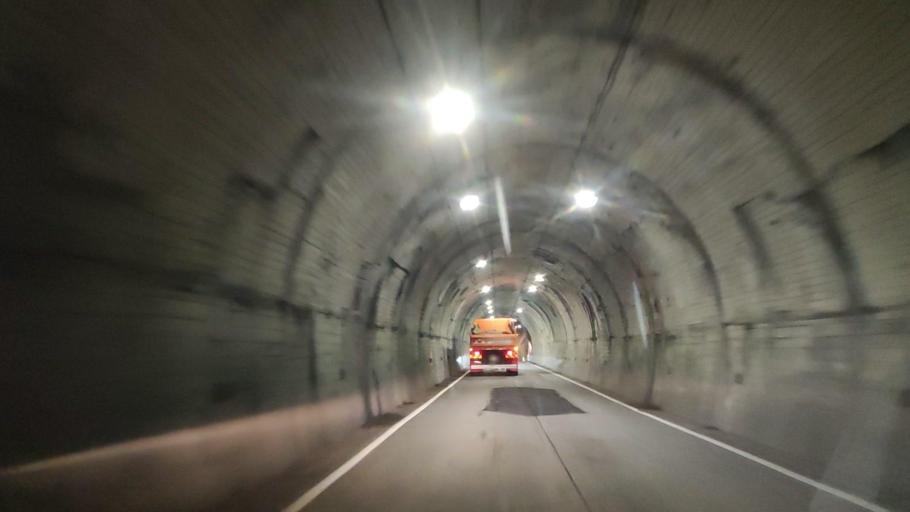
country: JP
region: Nagano
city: Iiyama
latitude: 36.8765
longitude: 138.3196
